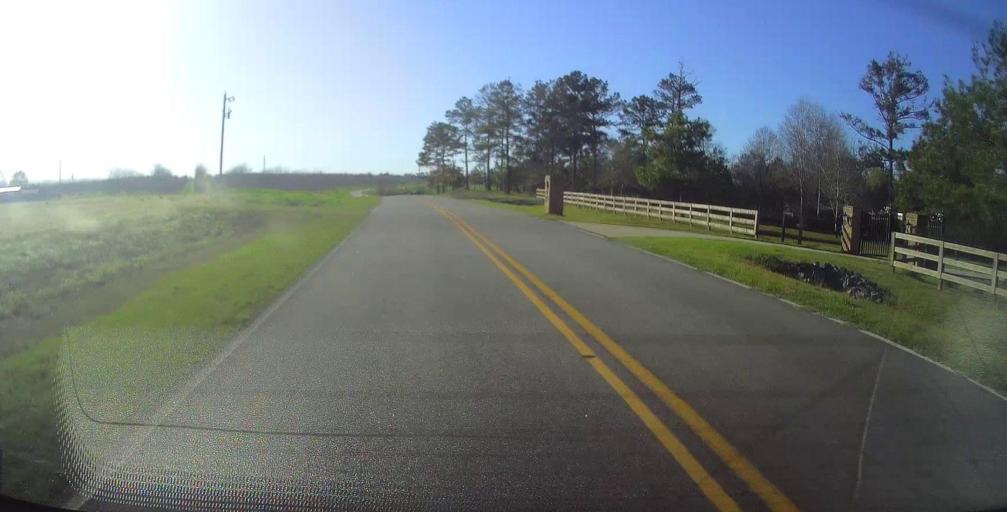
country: US
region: Georgia
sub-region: Dooly County
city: Unadilla
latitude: 32.3511
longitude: -83.6241
